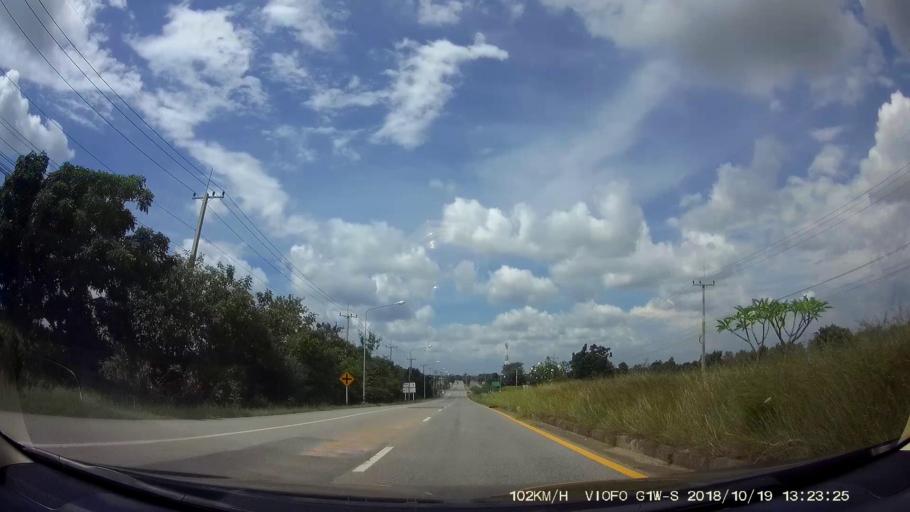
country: TH
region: Chaiyaphum
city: Chatturat
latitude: 15.4915
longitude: 101.8215
